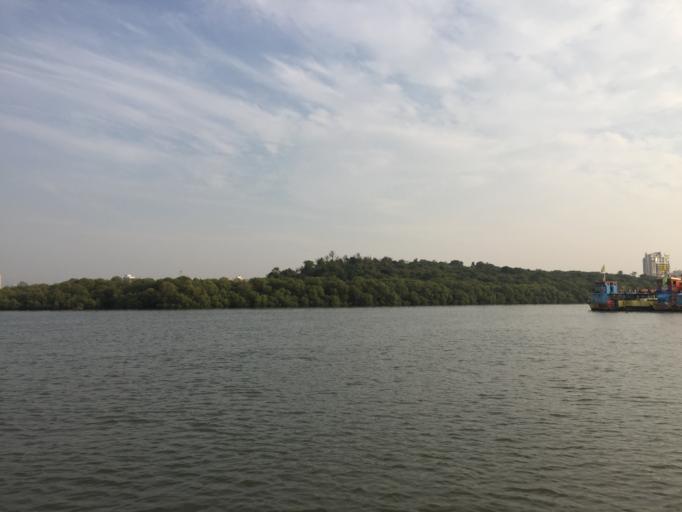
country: IN
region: Maharashtra
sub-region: Mumbai Suburban
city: Borivli
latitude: 19.2247
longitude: 72.8117
